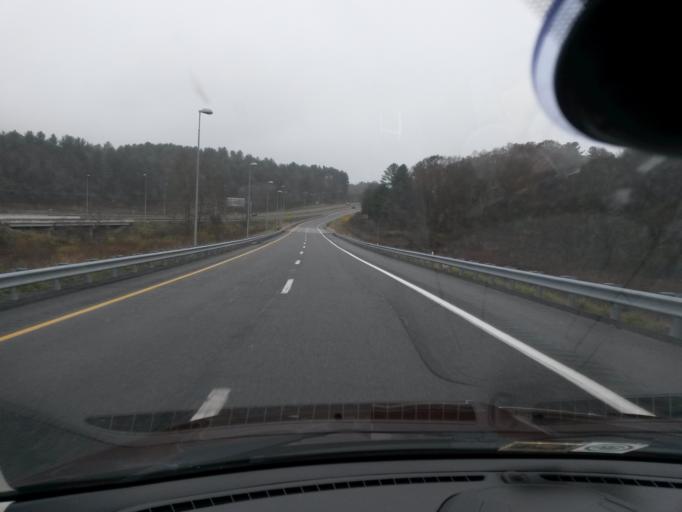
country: US
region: Virginia
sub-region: Carroll County
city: Hillsville
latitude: 36.7515
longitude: -80.7548
